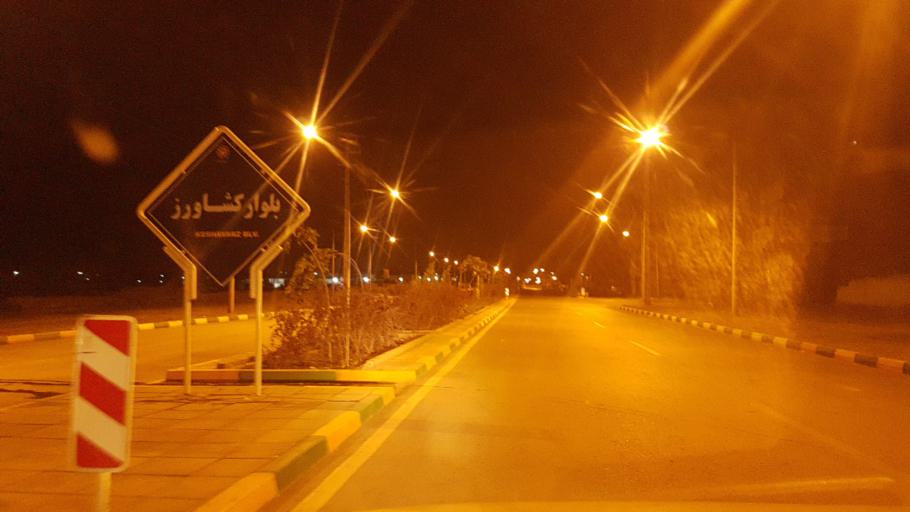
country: IR
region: Razavi Khorasan
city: Mashhad
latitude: 36.3559
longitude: 59.5665
